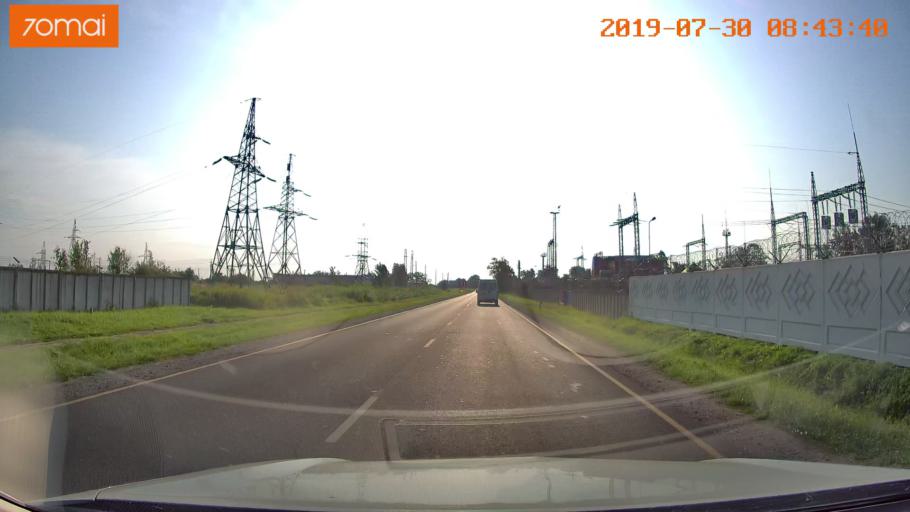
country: RU
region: Kaliningrad
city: Chernyakhovsk
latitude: 54.6268
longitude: 21.8446
